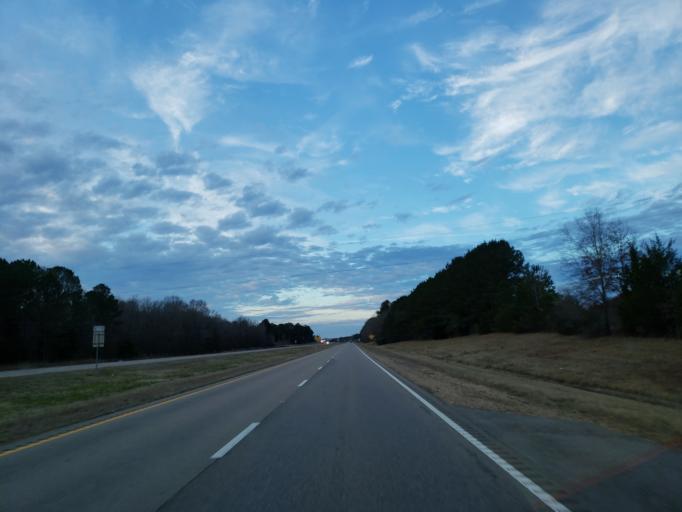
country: US
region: Mississippi
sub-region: Kemper County
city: De Kalb
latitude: 32.8207
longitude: -88.4590
